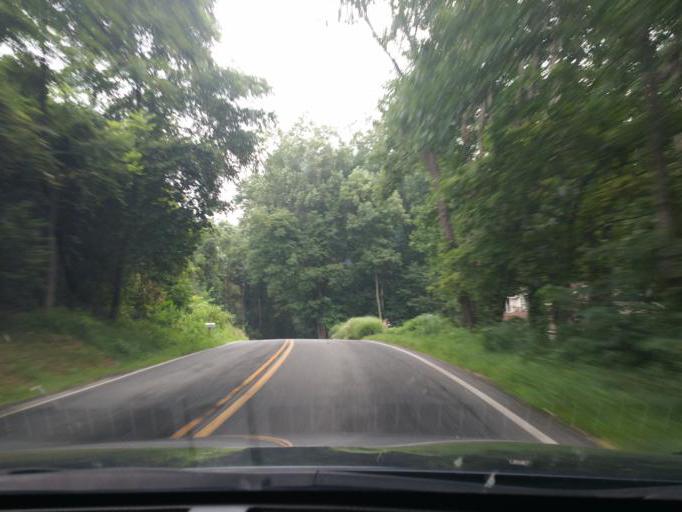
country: US
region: Maryland
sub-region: Cecil County
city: Rising Sun
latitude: 39.6576
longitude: -76.1463
